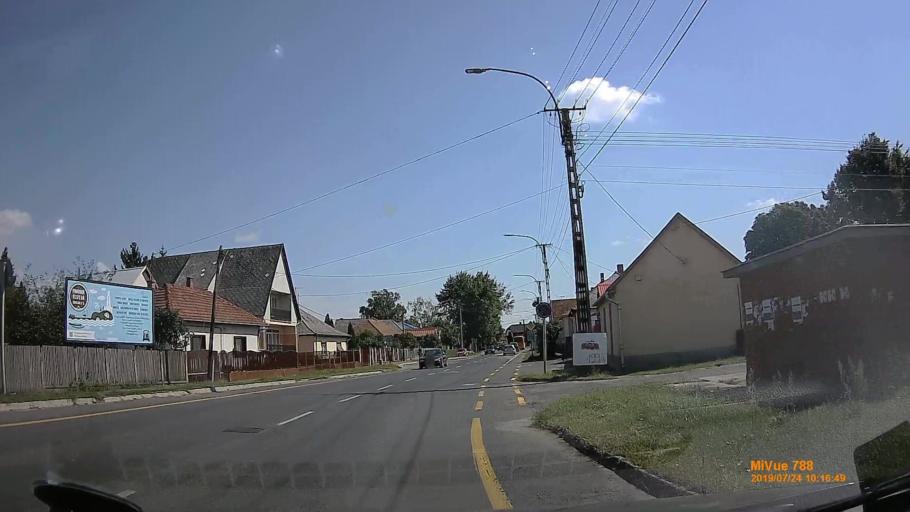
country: HU
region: Szabolcs-Szatmar-Bereg
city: Vasarosnameny
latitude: 48.1215
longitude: 22.3151
